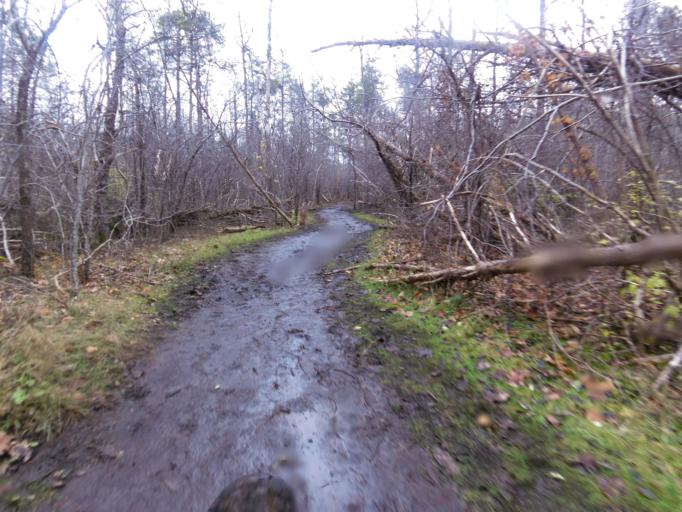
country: CA
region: Ontario
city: Bells Corners
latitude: 45.2985
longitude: -75.8062
